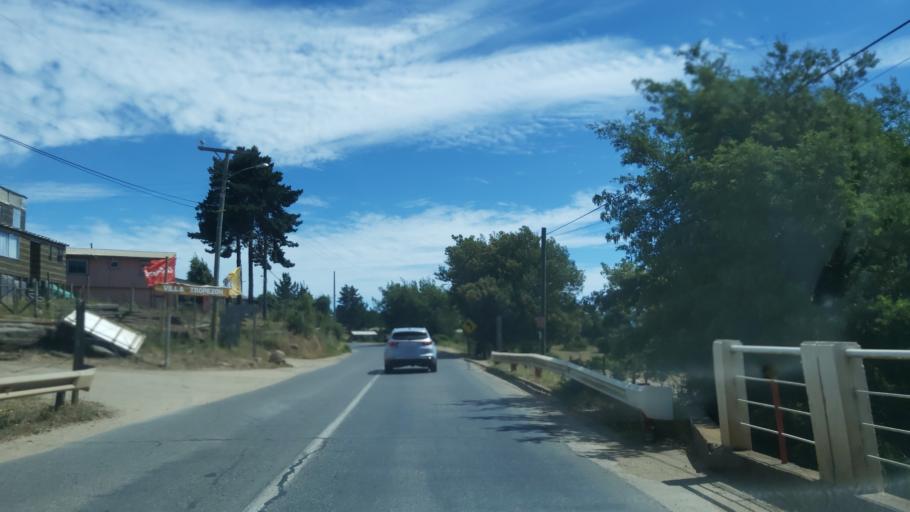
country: CL
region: Maule
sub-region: Provincia de Talca
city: Constitucion
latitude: -35.5038
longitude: -72.5191
